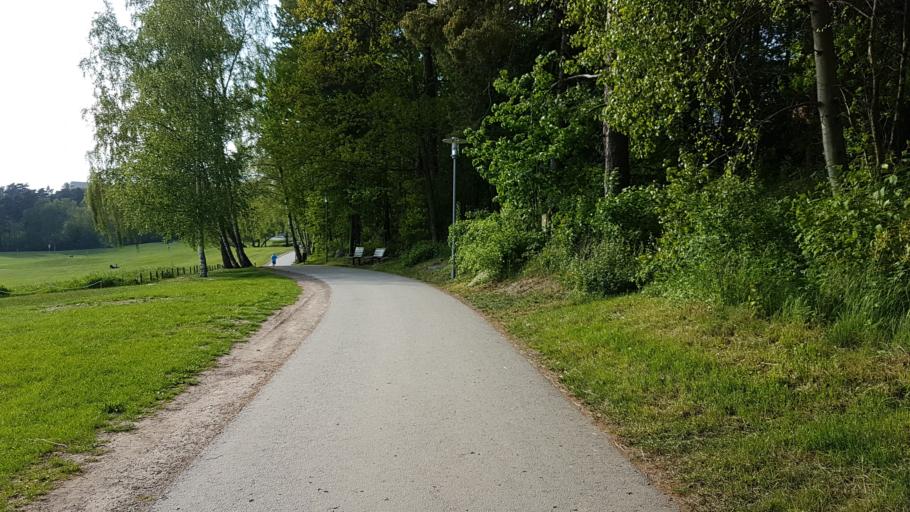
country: SE
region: Stockholm
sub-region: Solna Kommun
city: Rasunda
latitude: 59.3721
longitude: 17.9758
